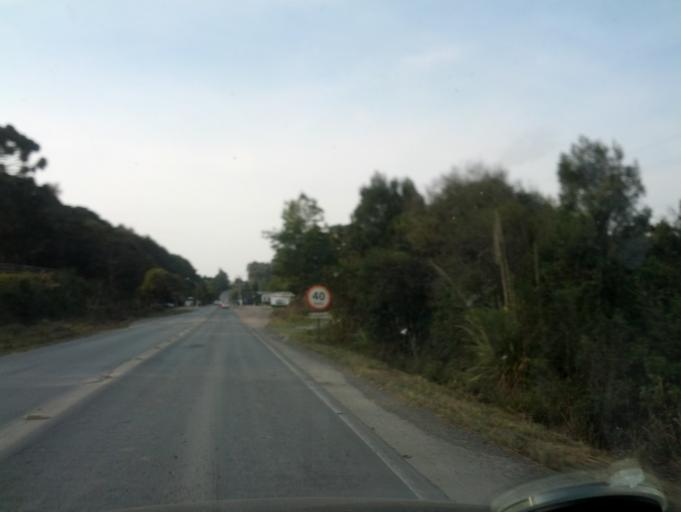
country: BR
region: Santa Catarina
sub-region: Otacilio Costa
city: Otacilio Costa
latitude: -27.5917
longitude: -50.1683
